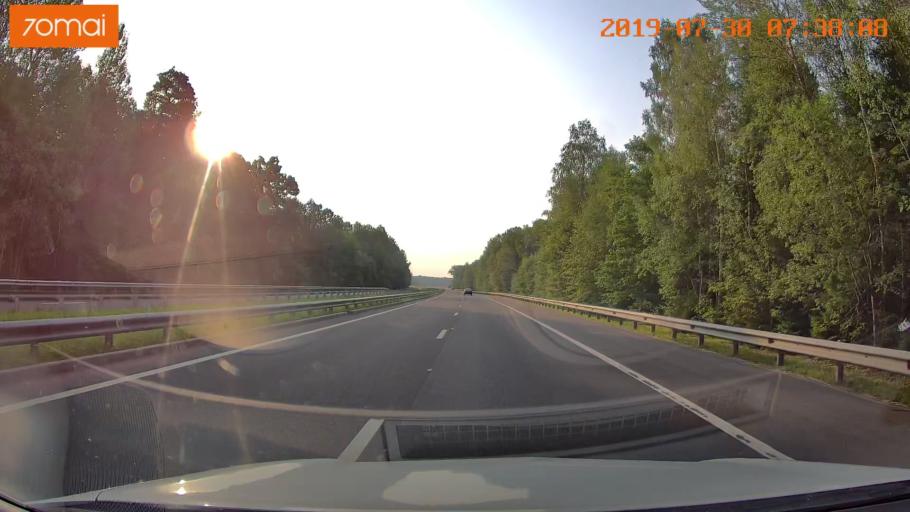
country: RU
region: Kaliningrad
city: Gvardeysk
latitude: 54.6513
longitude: 21.1604
